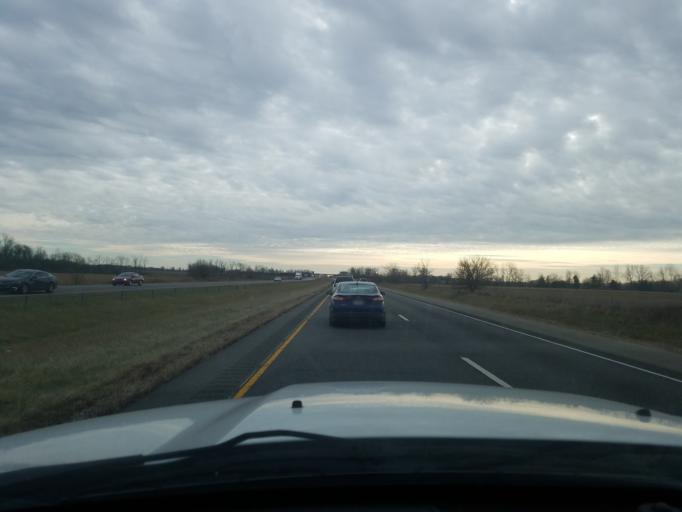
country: US
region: Indiana
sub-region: Grant County
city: Fairmount
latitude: 40.3381
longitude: -85.5593
